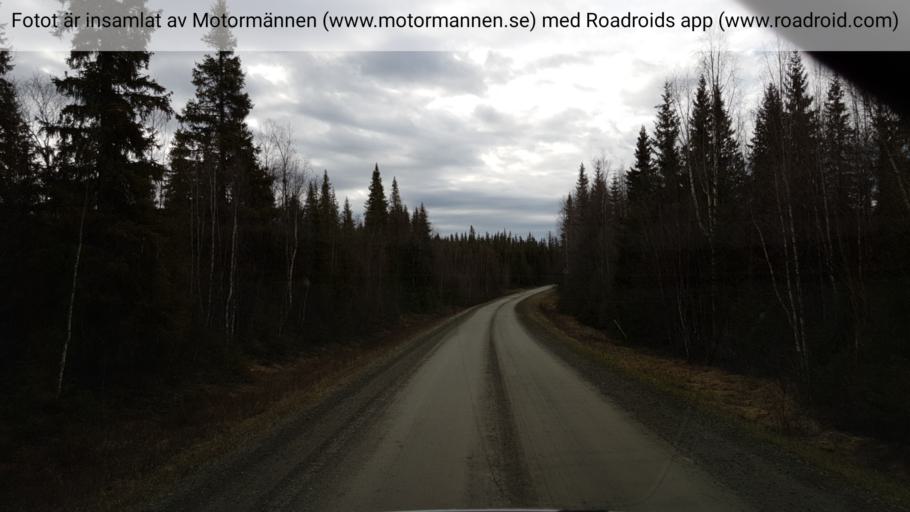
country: SE
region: Vaesterbotten
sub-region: Vilhelmina Kommun
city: Sjoberg
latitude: 65.5537
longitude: 15.4103
